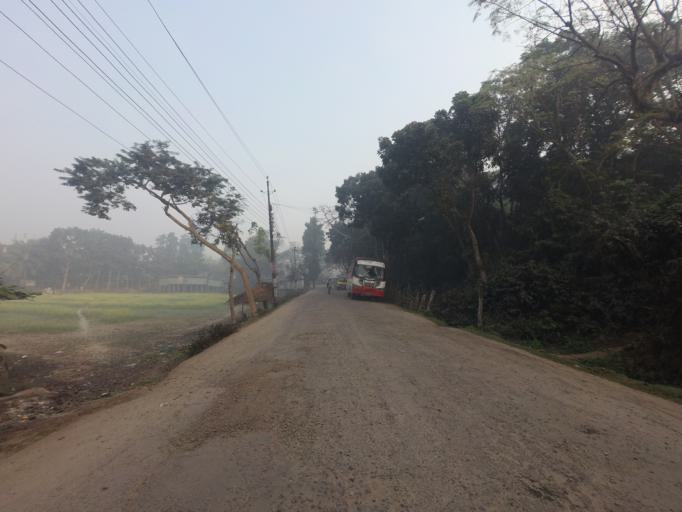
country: BD
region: Khulna
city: Narail
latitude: 23.1647
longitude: 89.4955
